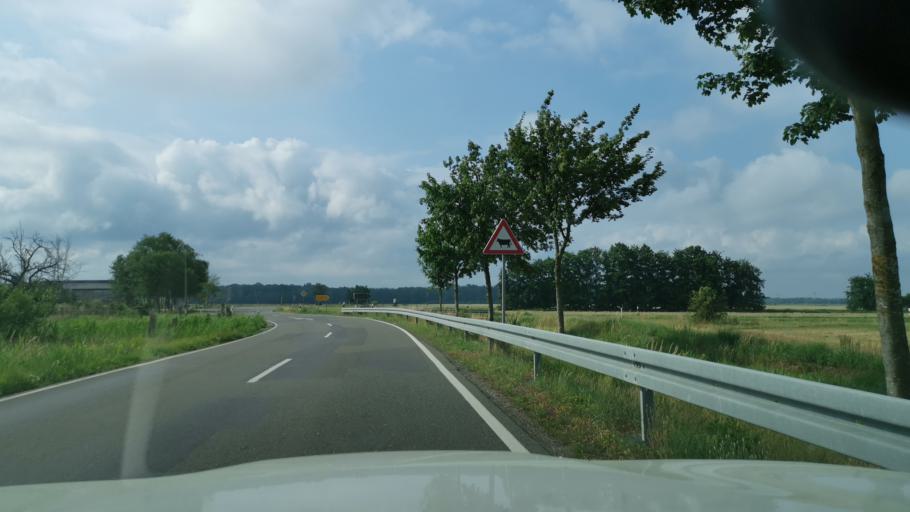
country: DE
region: Saxony-Anhalt
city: Annaburg
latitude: 51.7640
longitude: 13.0313
